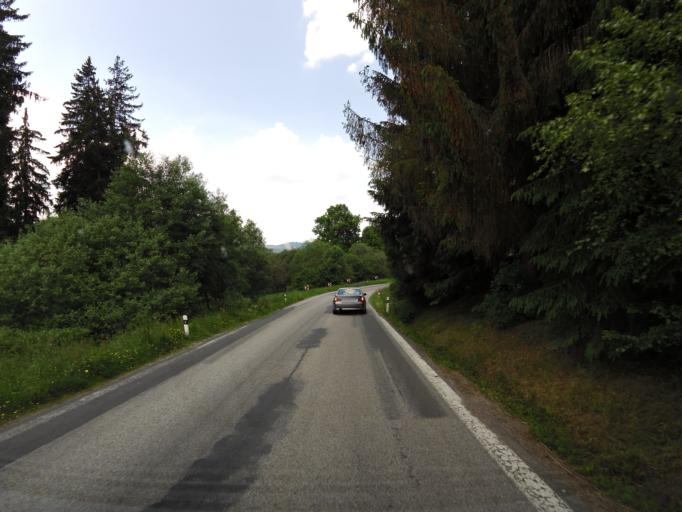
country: CZ
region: Jihocesky
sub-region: Okres Cesky Krumlov
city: Horni Plana
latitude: 48.8060
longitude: 13.9705
